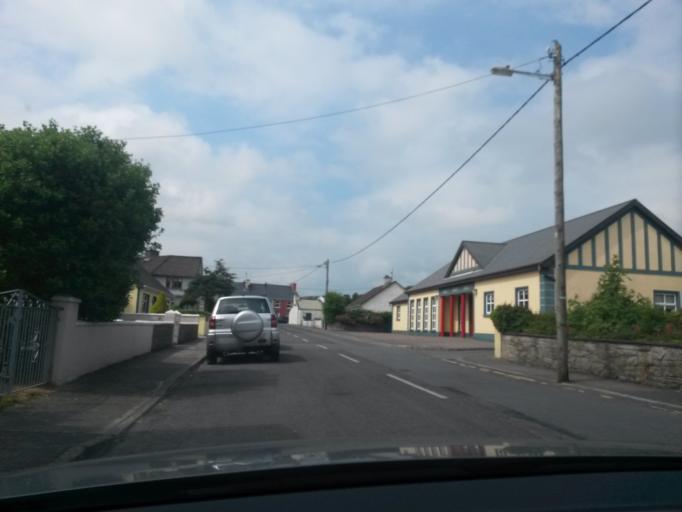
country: IE
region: Munster
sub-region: An Clar
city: Kilrush
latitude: 52.6373
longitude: -9.4892
